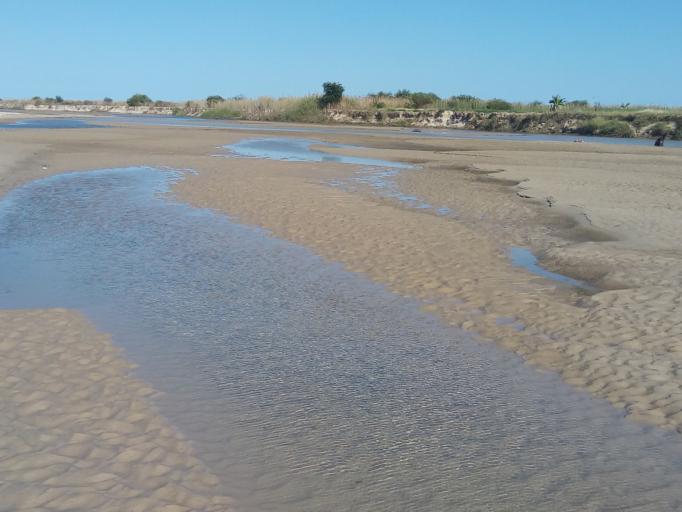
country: MG
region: Menabe
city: Morondava
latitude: -20.3346
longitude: 44.3128
